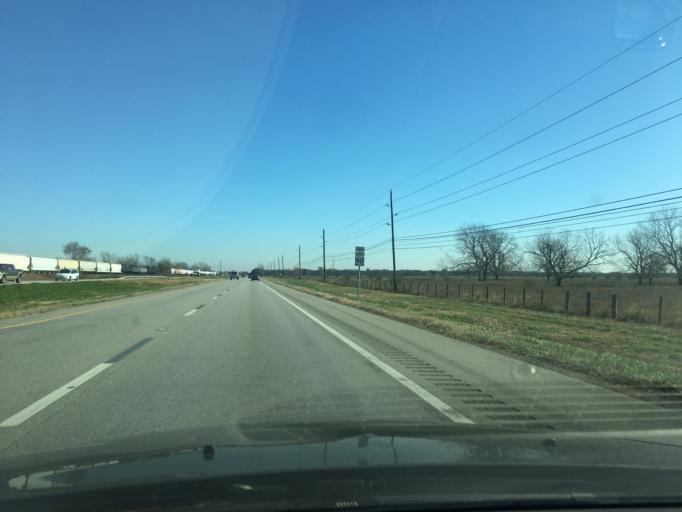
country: US
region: Texas
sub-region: Fort Bend County
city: New Territory
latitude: 29.5989
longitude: -95.7104
